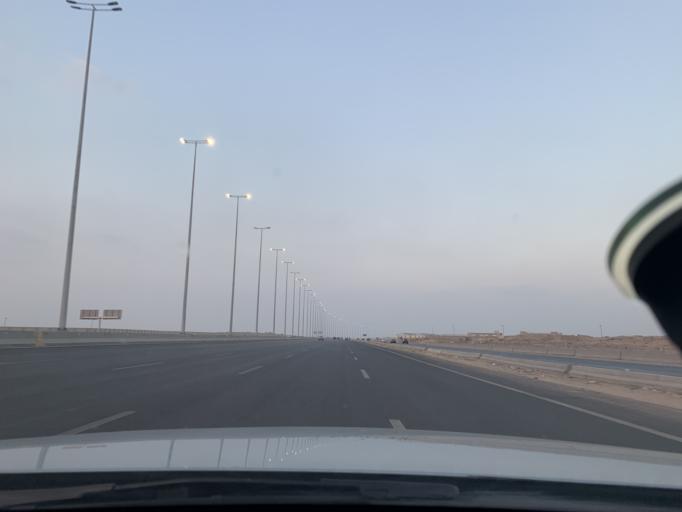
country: EG
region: Muhafazat al Qalyubiyah
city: Al Khankah
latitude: 30.0854
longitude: 31.4557
